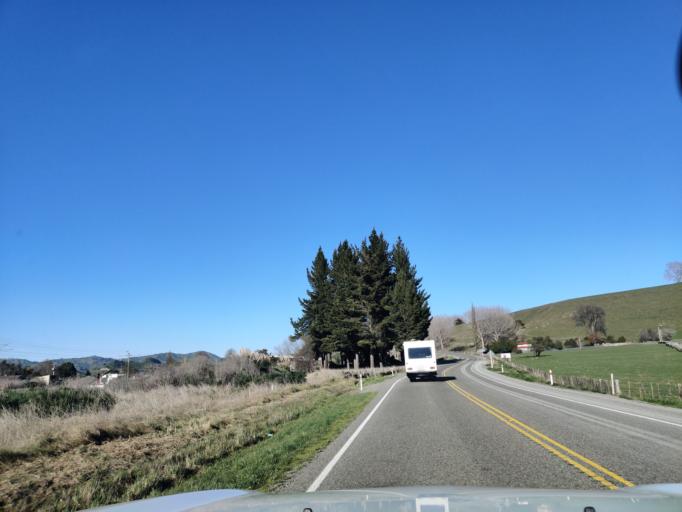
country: NZ
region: Manawatu-Wanganui
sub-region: Ruapehu District
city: Waiouru
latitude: -39.7345
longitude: 175.8430
